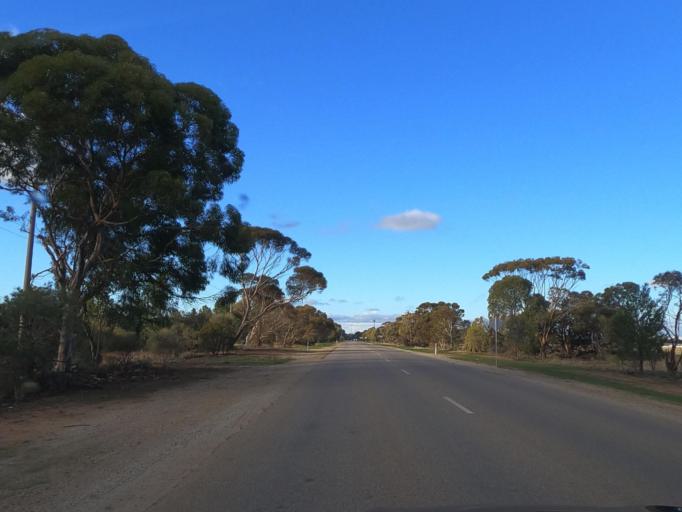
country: AU
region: Victoria
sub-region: Swan Hill
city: Swan Hill
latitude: -35.3451
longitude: 143.5251
